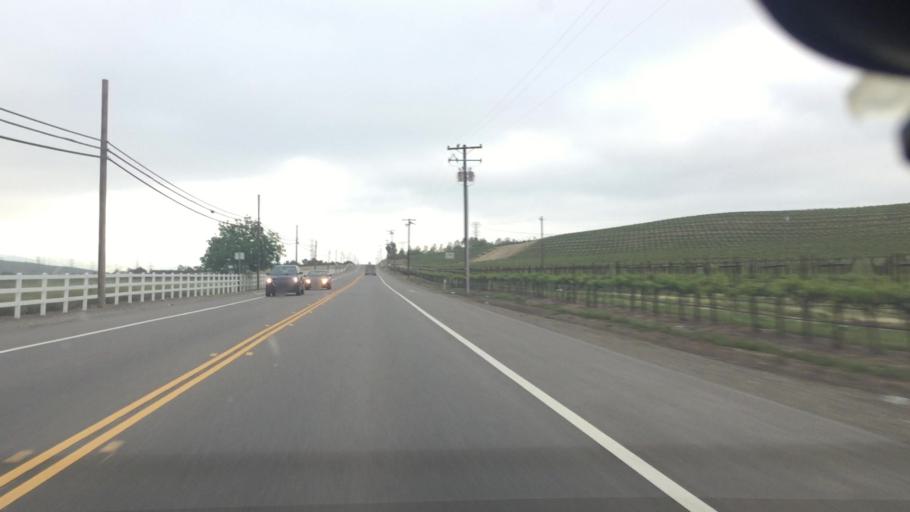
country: US
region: California
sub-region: Alameda County
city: Livermore
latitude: 37.6651
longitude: -121.7073
